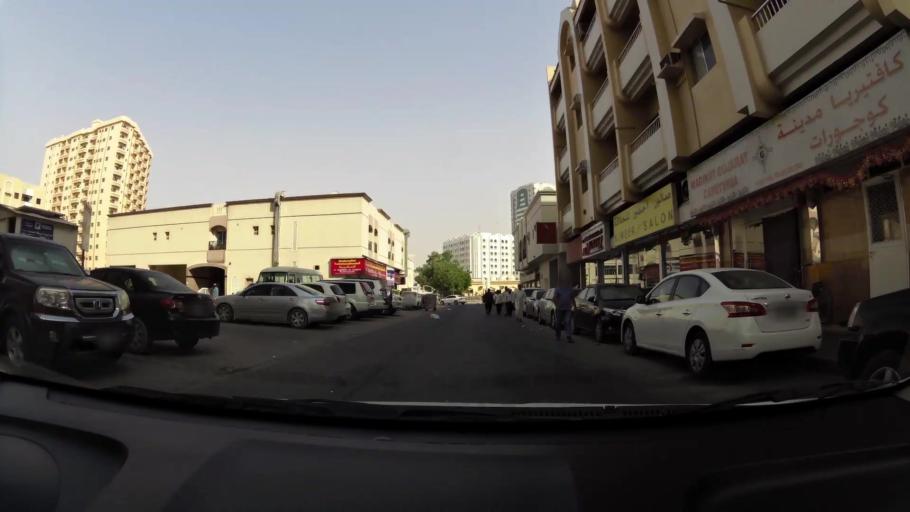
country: AE
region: Ash Shariqah
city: Sharjah
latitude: 25.3326
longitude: 55.3949
